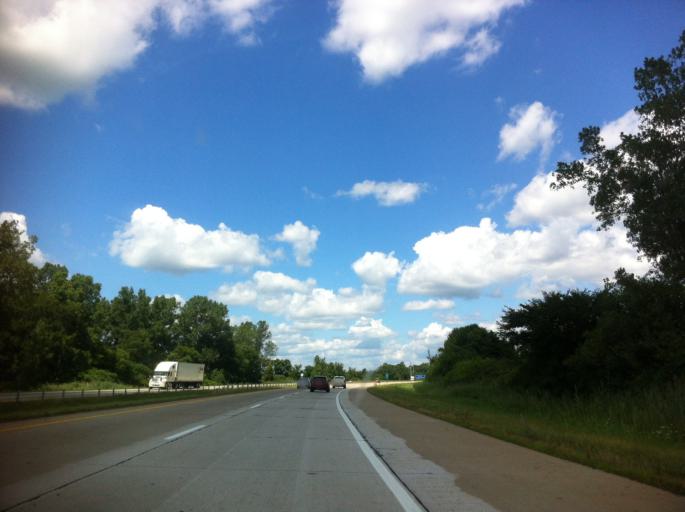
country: US
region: Michigan
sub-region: Monroe County
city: Lambertville
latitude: 41.8236
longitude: -83.6838
